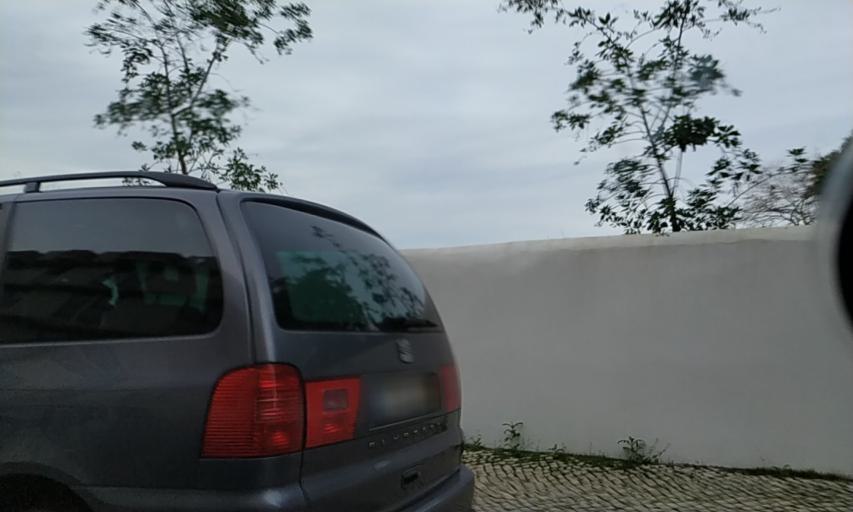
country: PT
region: Setubal
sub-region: Setubal
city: Setubal
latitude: 38.5311
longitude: -8.8834
